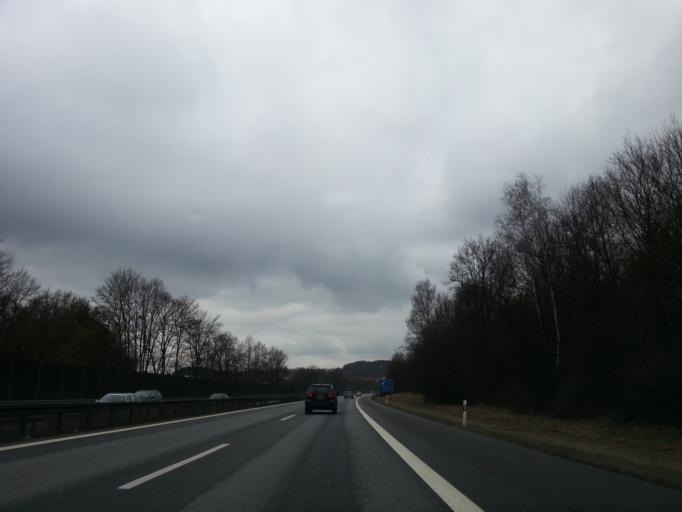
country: DE
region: Bavaria
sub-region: Upper Palatinate
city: Nittendorf
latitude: 49.0207
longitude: 11.9644
